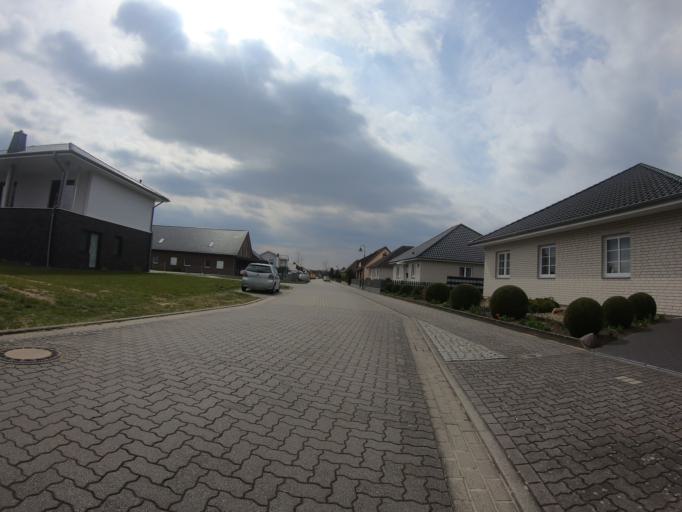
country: DE
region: Lower Saxony
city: Hankensbuttel
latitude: 52.7219
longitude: 10.5985
